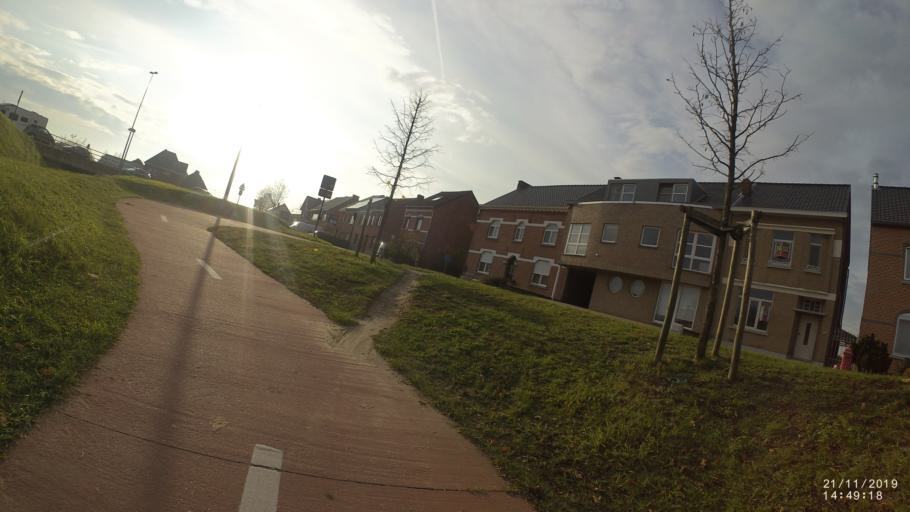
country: BE
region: Flanders
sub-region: Provincie Limburg
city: Hasselt
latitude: 50.9130
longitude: 5.3223
